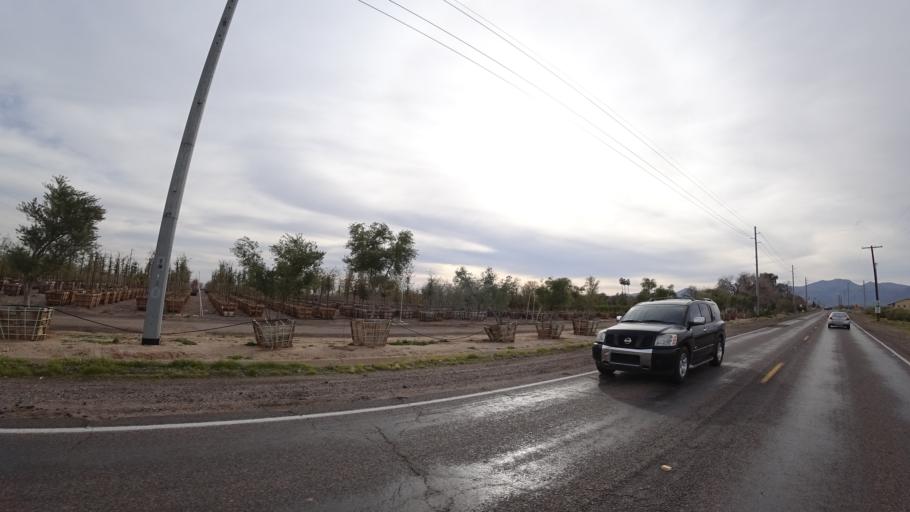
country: US
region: Arizona
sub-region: Maricopa County
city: Citrus Park
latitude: 33.5662
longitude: -112.4236
